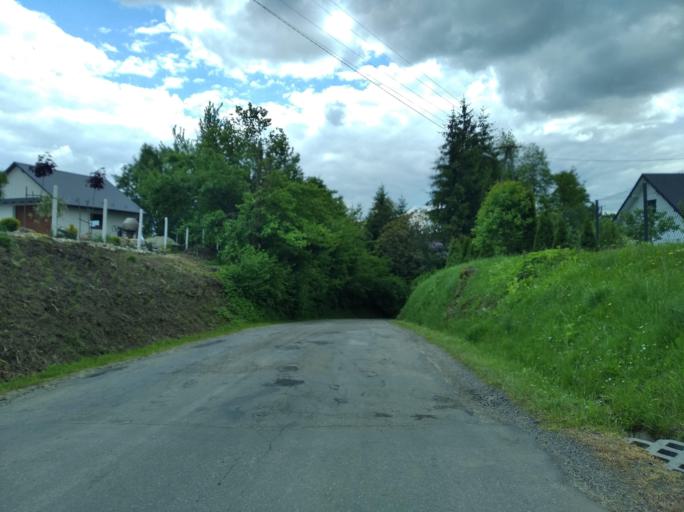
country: PL
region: Subcarpathian Voivodeship
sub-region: Powiat brzozowski
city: Jasionow
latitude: 49.6620
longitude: 21.9747
